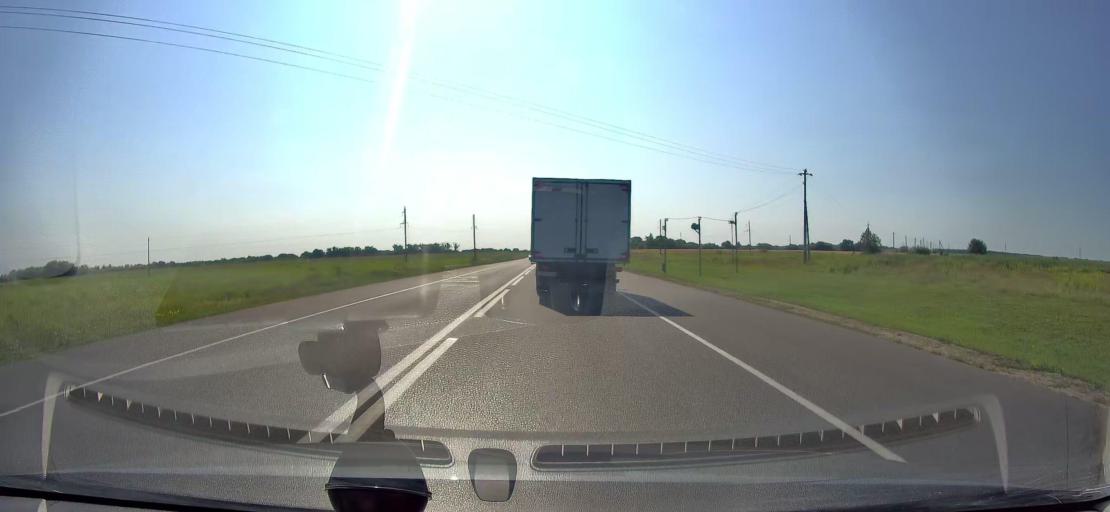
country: RU
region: Orjol
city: Kromy
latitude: 52.6529
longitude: 35.7269
